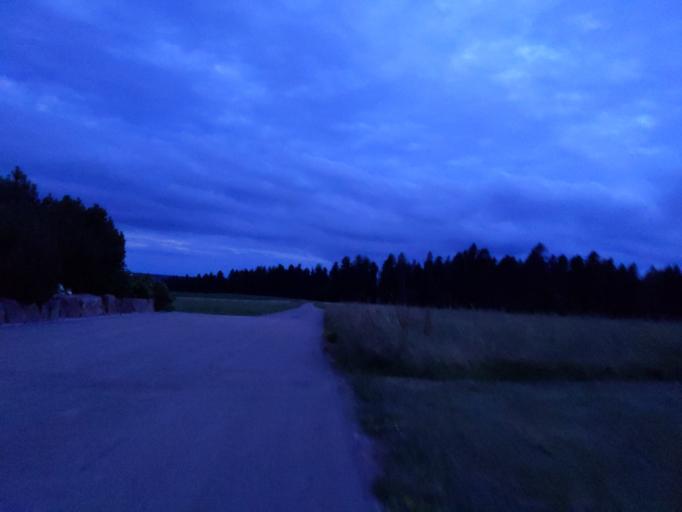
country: DE
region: Baden-Wuerttemberg
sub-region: Karlsruhe Region
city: Alpirsbach
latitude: 48.3349
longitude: 8.4315
